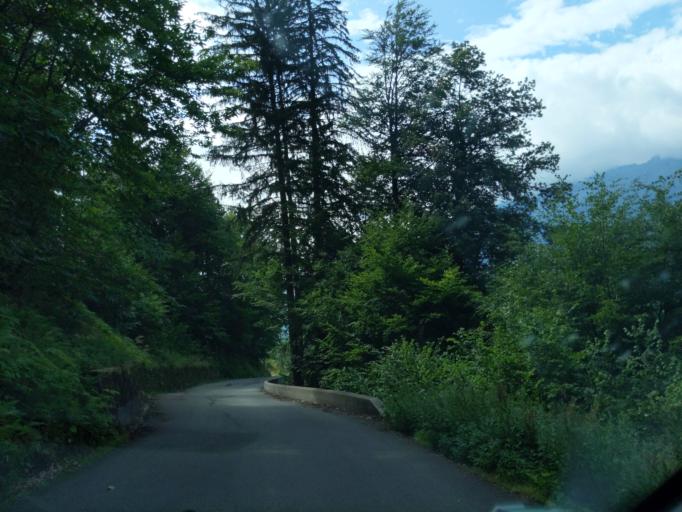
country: FR
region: Rhone-Alpes
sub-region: Departement de la Savoie
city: Ugine
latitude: 45.7478
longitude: 6.4550
